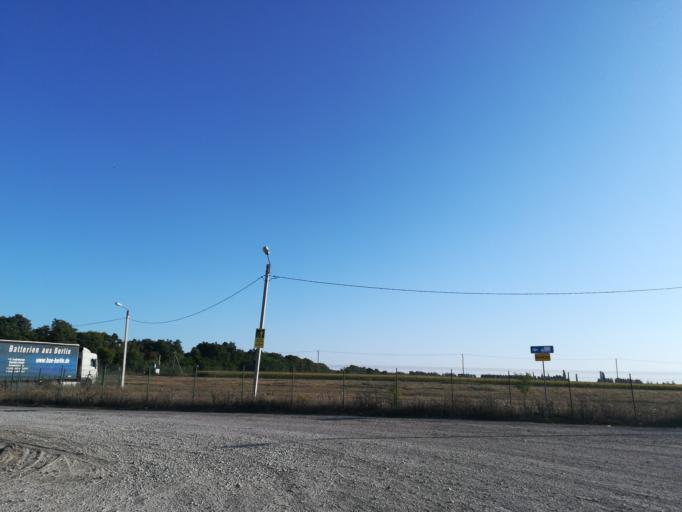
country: RU
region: Belgorod
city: Bekhteyevka
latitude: 50.7933
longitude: 37.1440
